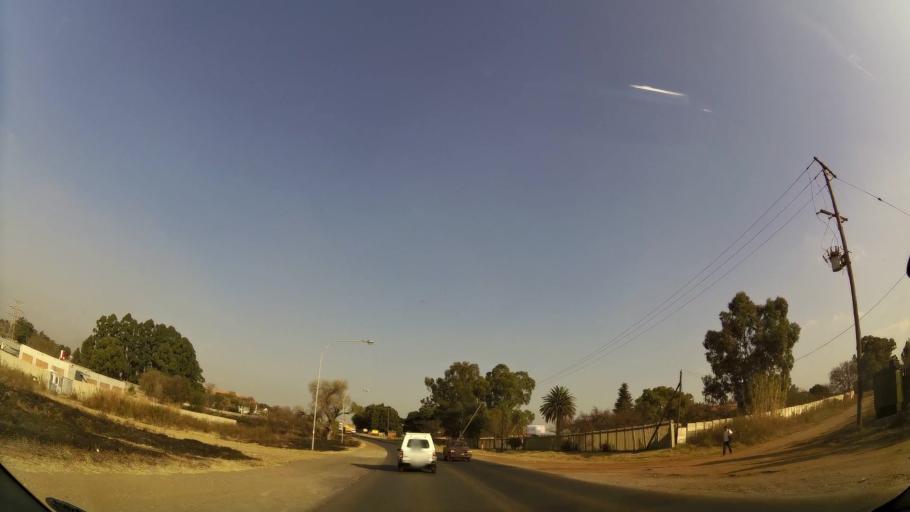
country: ZA
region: Gauteng
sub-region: Ekurhuleni Metropolitan Municipality
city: Benoni
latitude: -26.1357
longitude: 28.3901
